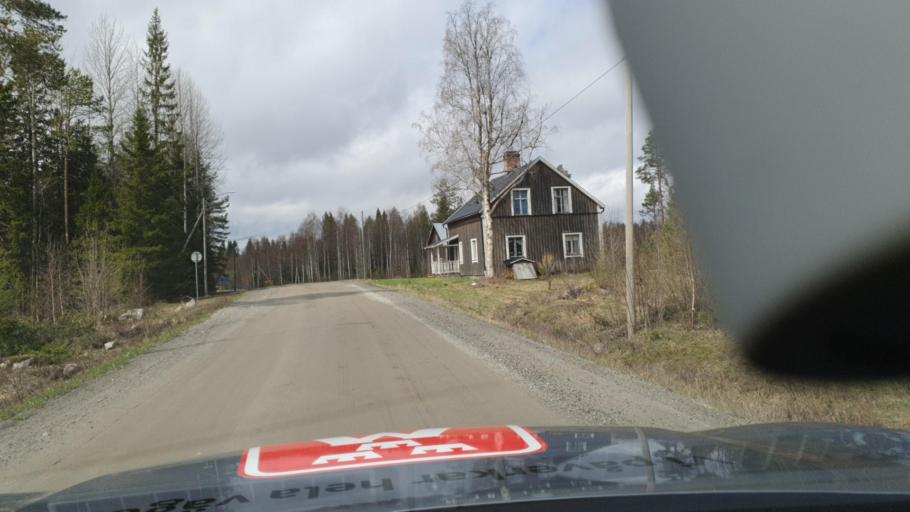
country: SE
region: Vaesterbotten
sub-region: Bjurholms Kommun
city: Bjurholm
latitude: 63.6981
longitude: 18.9487
